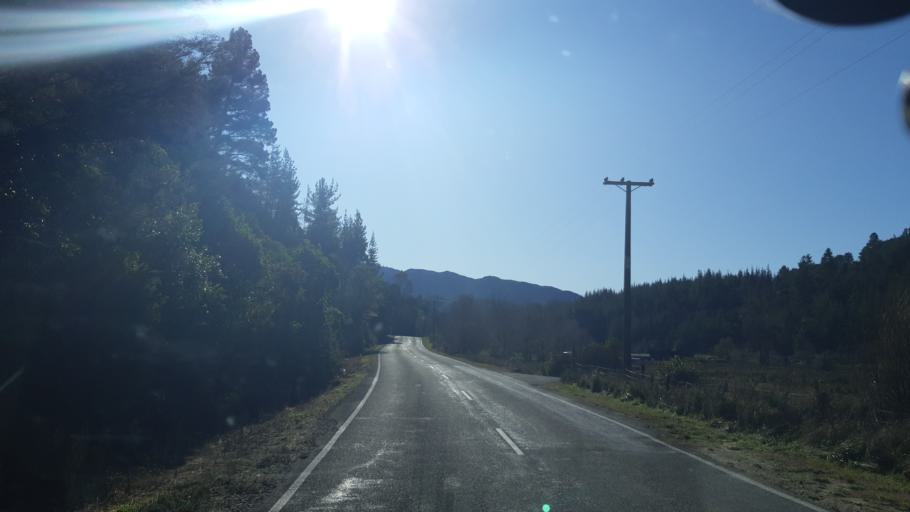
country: NZ
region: Tasman
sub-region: Tasman District
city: Motueka
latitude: -41.0251
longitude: 172.9794
